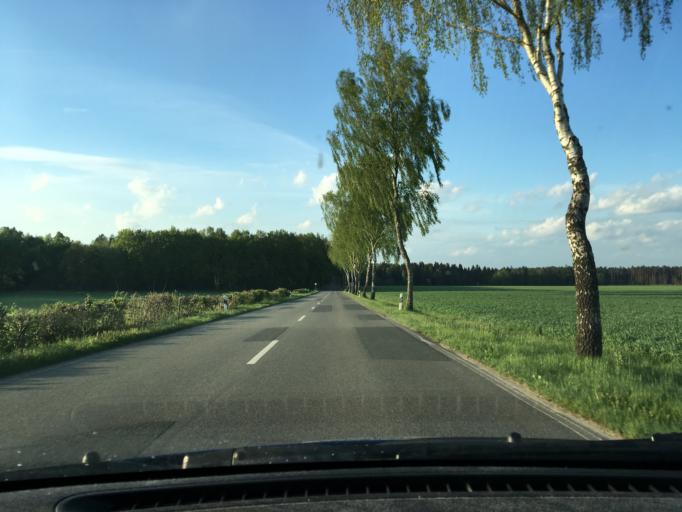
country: DE
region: Lower Saxony
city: Bergen
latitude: 52.8593
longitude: 9.9800
